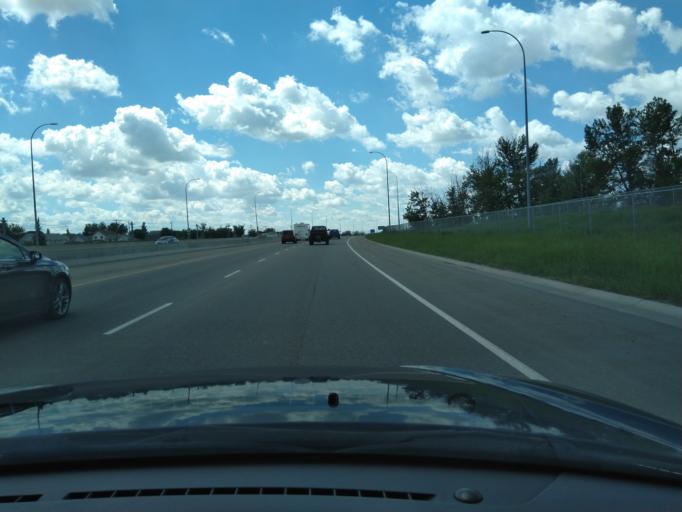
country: CA
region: Alberta
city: Calgary
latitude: 51.1170
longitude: -113.9707
